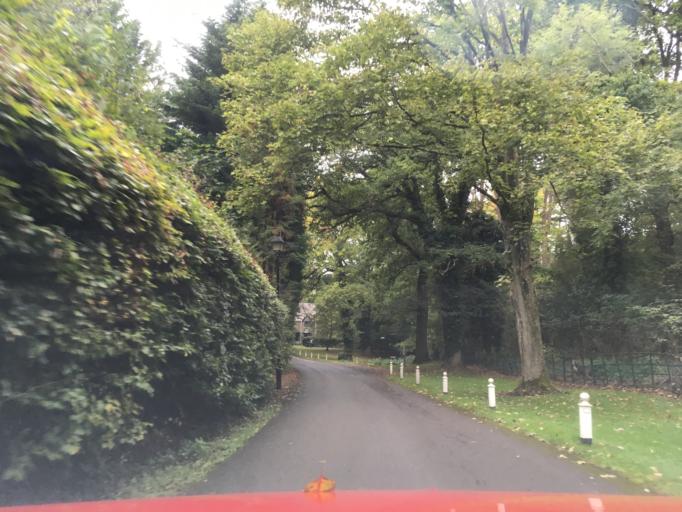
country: GB
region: England
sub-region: South Gloucestershire
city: Falfield
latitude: 51.6306
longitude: -2.4375
